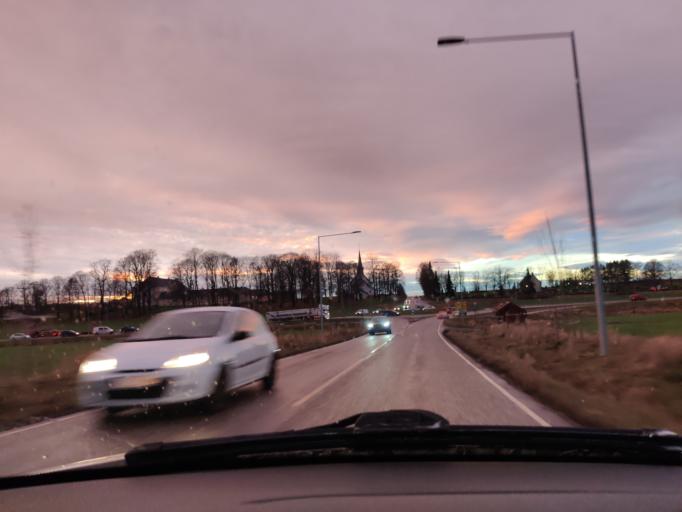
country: NO
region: Vestfold
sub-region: Tonsberg
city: Barkaker
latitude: 59.2925
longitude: 10.3920
